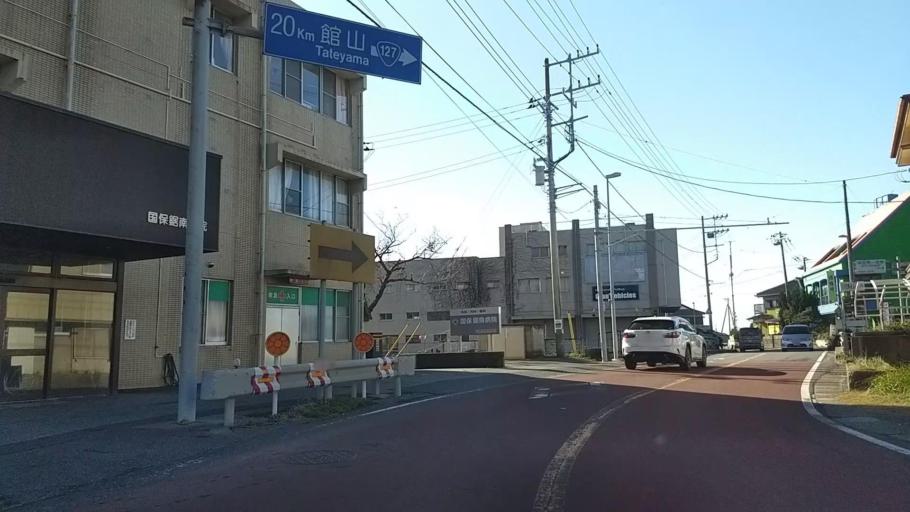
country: JP
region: Chiba
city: Tateyama
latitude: 35.1373
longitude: 139.8389
